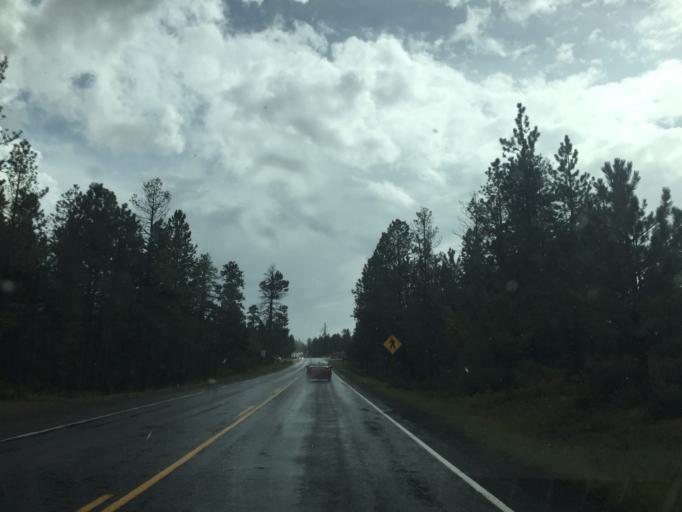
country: US
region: Utah
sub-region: Garfield County
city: Panguitch
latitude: 37.6575
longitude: -112.1619
